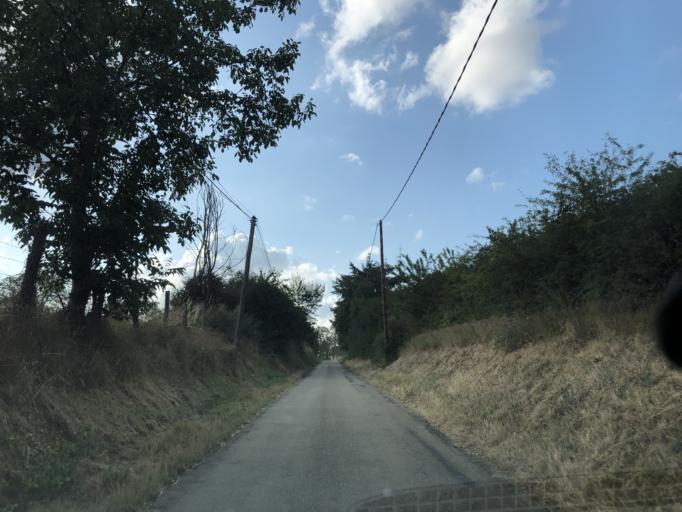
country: FR
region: Bourgogne
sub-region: Departement de l'Yonne
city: Charbuy
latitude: 47.8268
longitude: 3.4554
